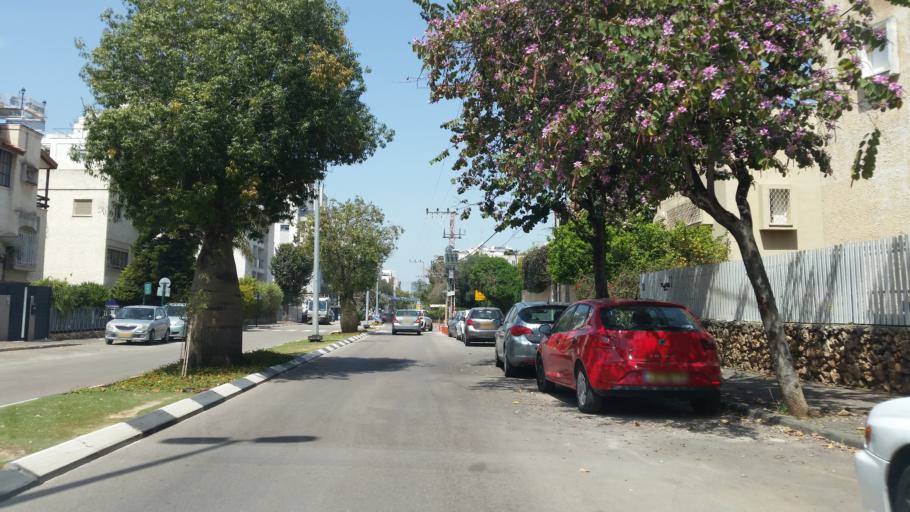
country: IL
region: Central District
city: Ra'anana
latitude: 32.1766
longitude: 34.8805
